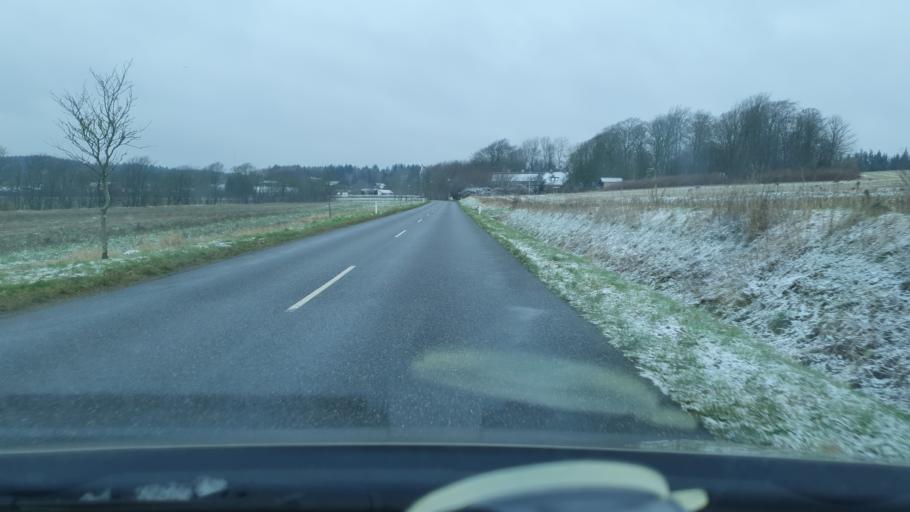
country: DK
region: North Denmark
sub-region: Jammerbugt Kommune
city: Brovst
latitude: 57.1294
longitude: 9.4724
